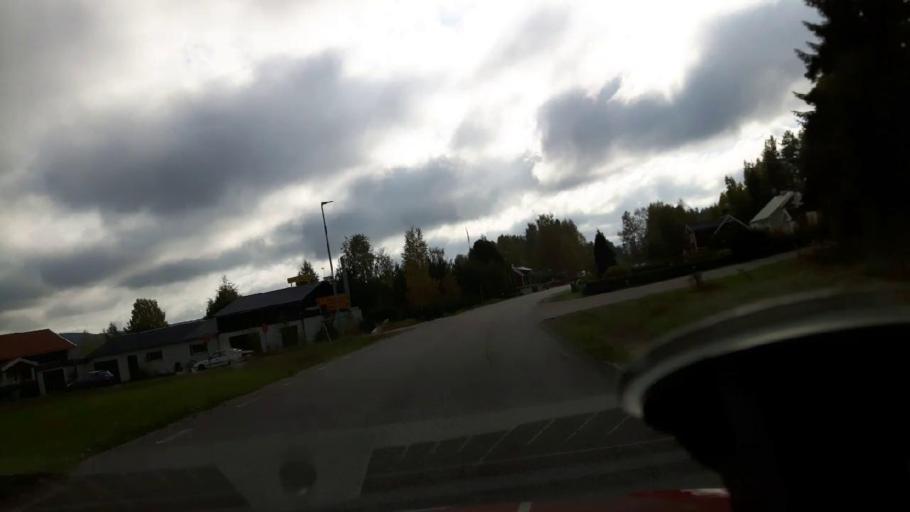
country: SE
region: Gaevleborg
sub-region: Ljusdals Kommun
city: Farila
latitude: 61.7984
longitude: 15.9096
